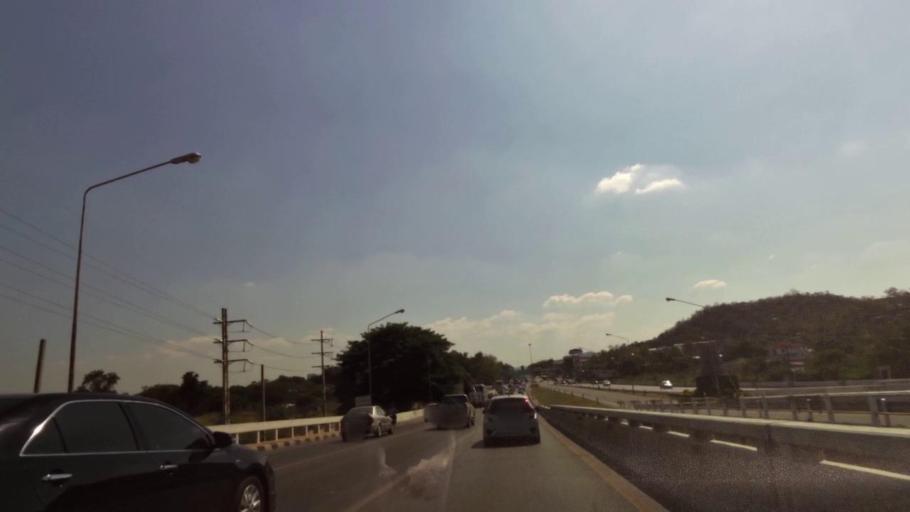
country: TH
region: Nakhon Sawan
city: Nakhon Sawan
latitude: 15.6868
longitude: 100.1242
